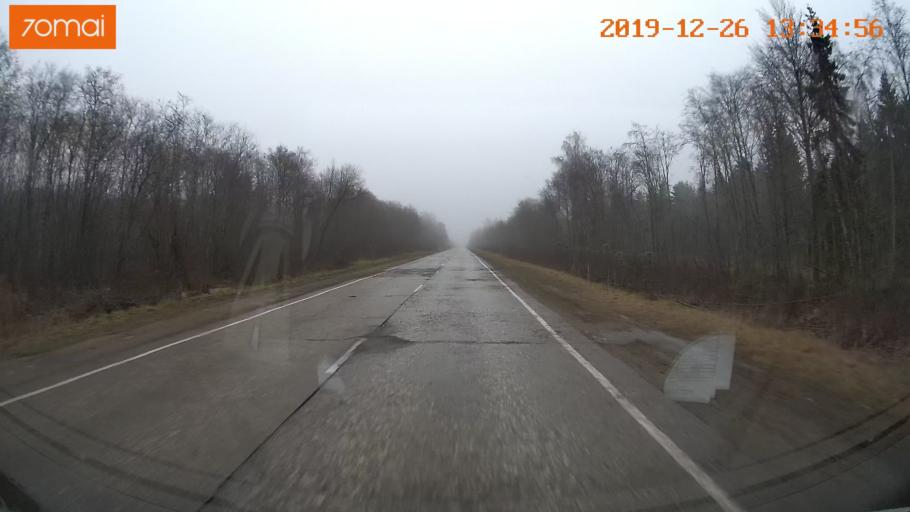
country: RU
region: Vologda
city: Sheksna
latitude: 58.7995
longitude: 38.3320
